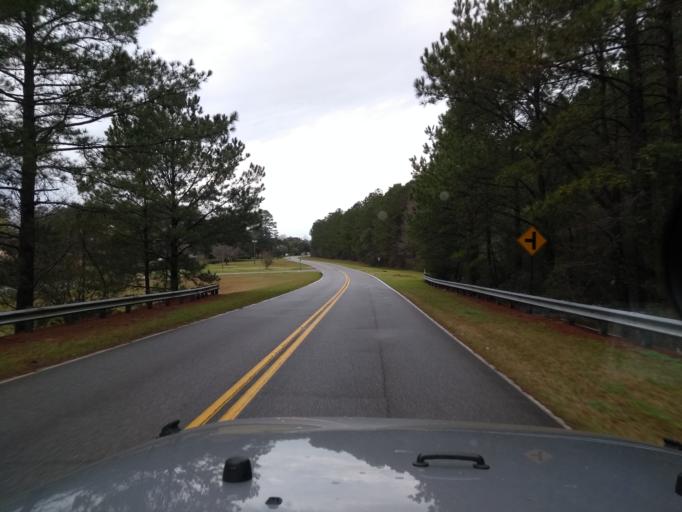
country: US
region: Georgia
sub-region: Chatham County
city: Georgetown
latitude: 32.0285
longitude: -81.1708
